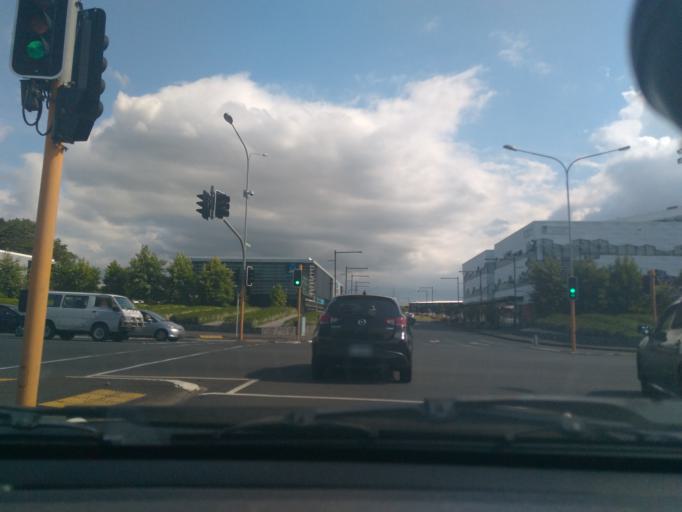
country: NZ
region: Auckland
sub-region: Auckland
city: Tamaki
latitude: -36.9363
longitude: 174.8760
